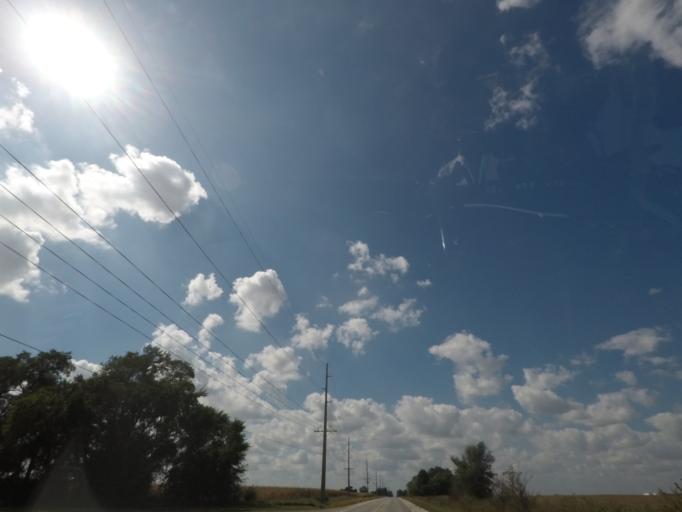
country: US
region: Iowa
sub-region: Story County
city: Nevada
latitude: 42.0231
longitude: -93.5304
